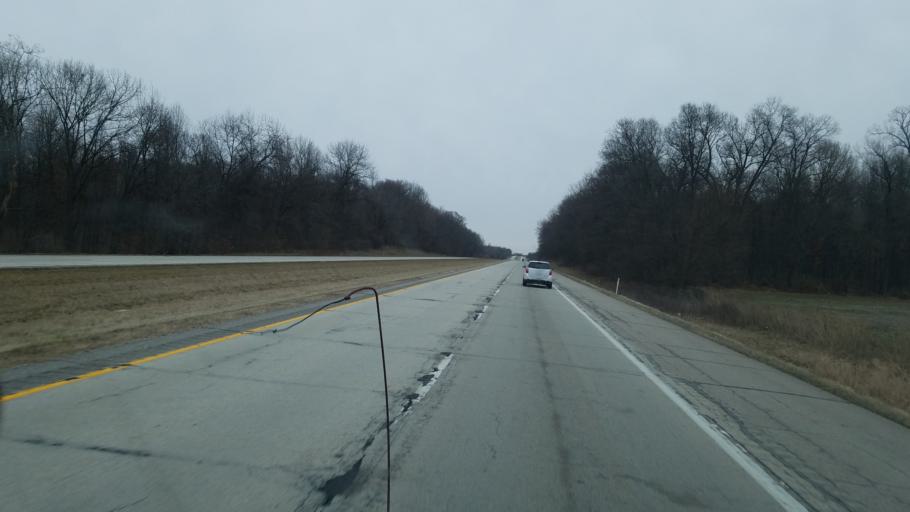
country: US
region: Indiana
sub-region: Starke County
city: Koontz Lake
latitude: 41.3644
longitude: -86.4182
